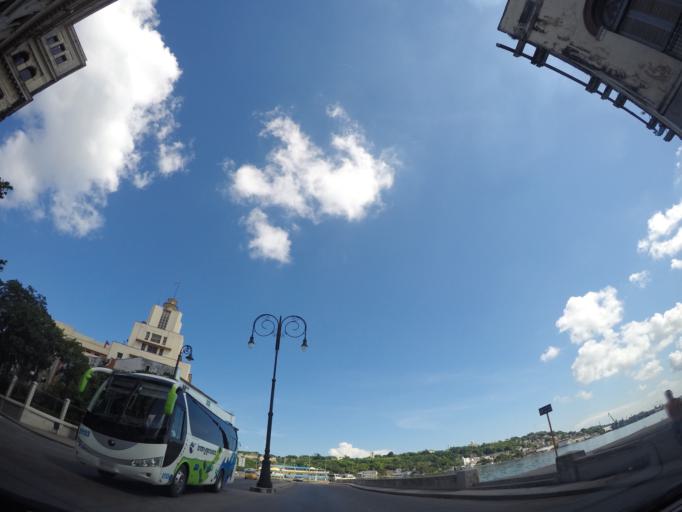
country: CU
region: La Habana
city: La Habana Vieja
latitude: 23.1382
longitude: -82.3481
